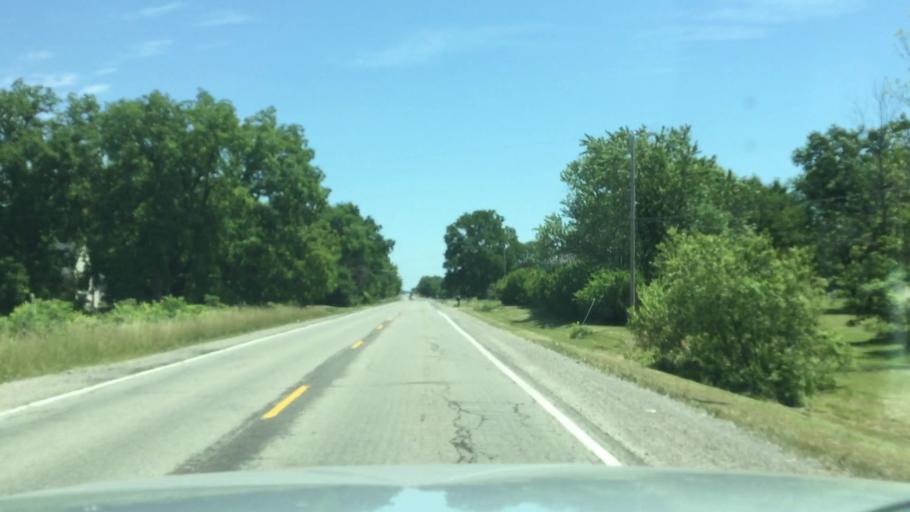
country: US
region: Michigan
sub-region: Genesee County
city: Swartz Creek
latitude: 42.9429
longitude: -83.7950
